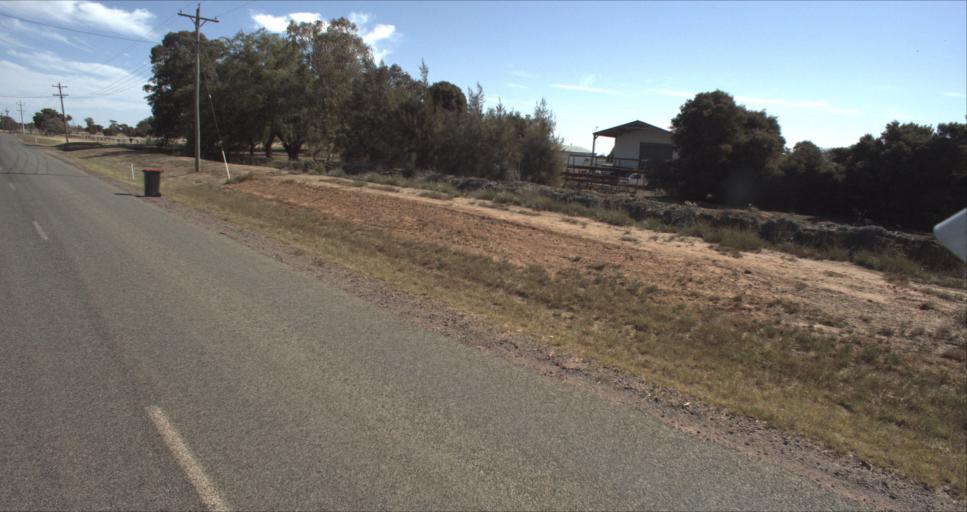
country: AU
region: New South Wales
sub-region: Leeton
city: Leeton
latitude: -34.5641
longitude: 146.3830
